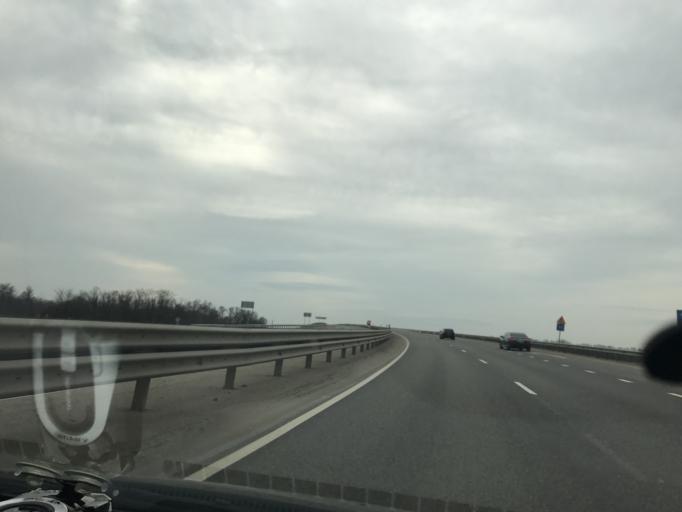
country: RU
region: Krasnodarskiy
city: Uspenskoye
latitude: 44.7984
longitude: 41.4579
